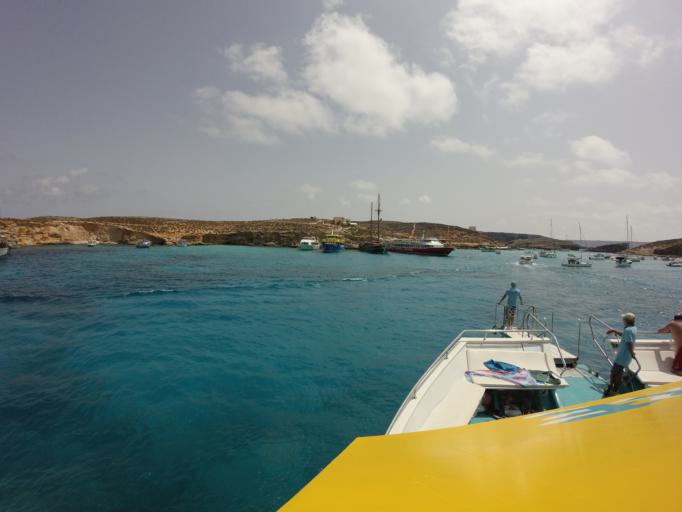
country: MT
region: Il-Qala
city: Qala
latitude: 36.0157
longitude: 14.3225
